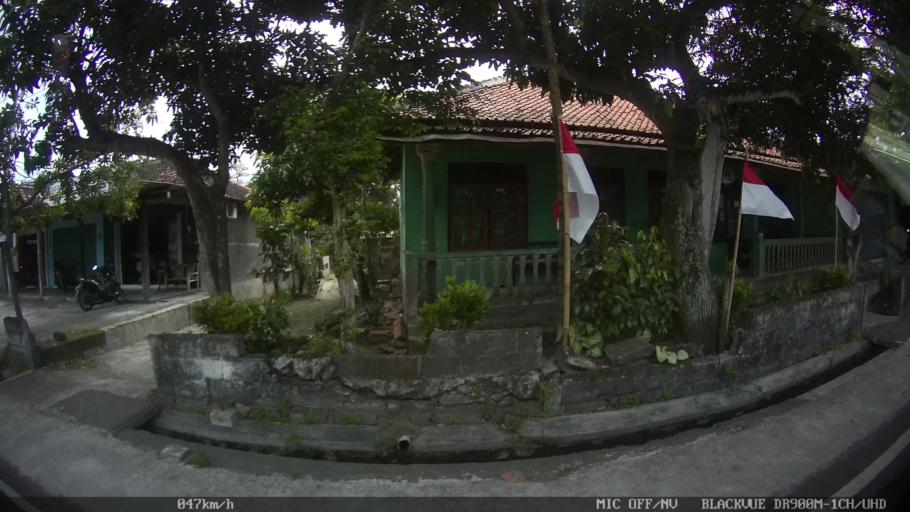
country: ID
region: Central Java
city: Candi Prambanan
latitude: -7.7650
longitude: 110.4885
